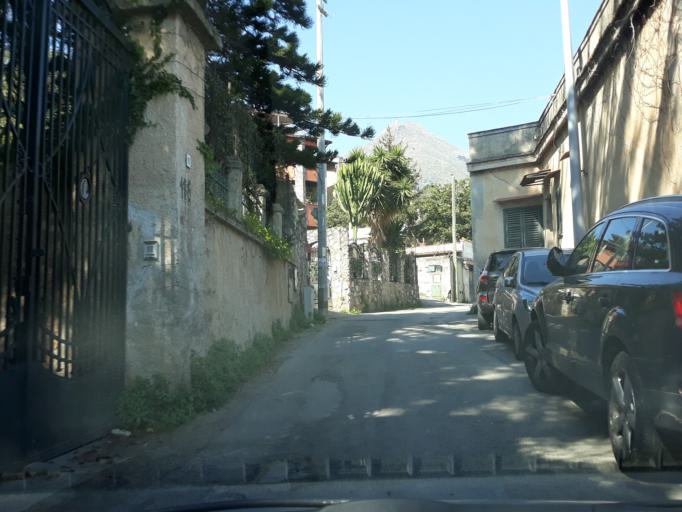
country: IT
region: Sicily
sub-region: Palermo
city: Piano dei Geli
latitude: 38.1094
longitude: 13.3017
